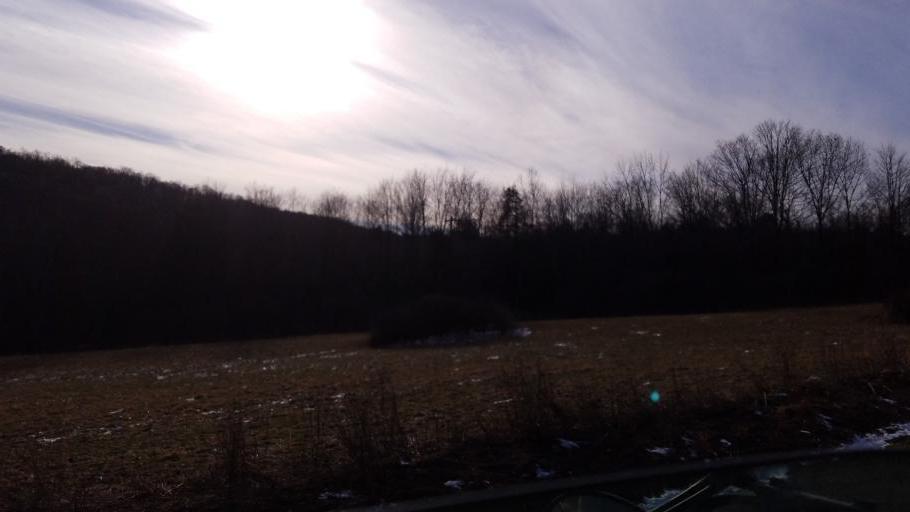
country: US
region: New York
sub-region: Allegany County
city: Andover
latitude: 42.1821
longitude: -77.8601
